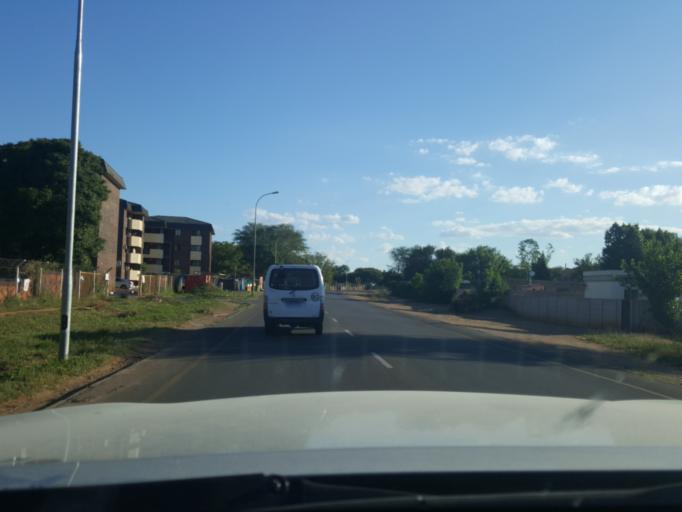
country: BW
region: South East
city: Gaborone
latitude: -24.6430
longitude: 25.9379
